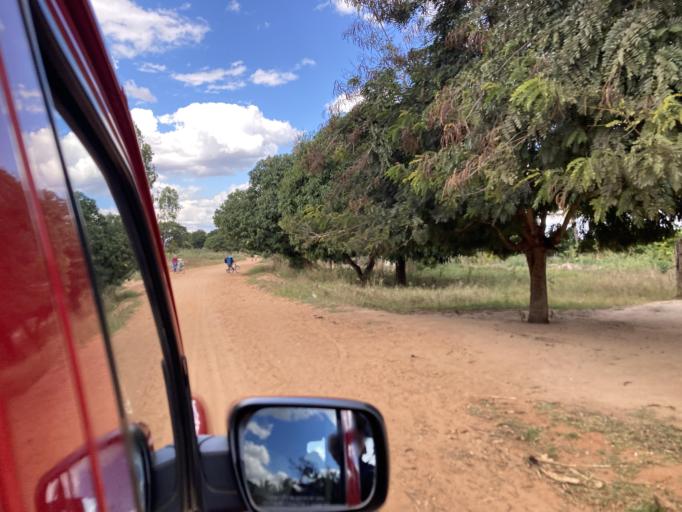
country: MZ
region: Cabo Delgado
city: Montepuez
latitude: -13.1251
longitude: 39.0276
